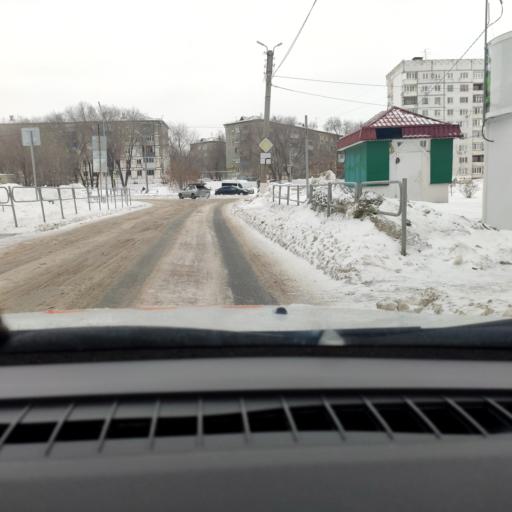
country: RU
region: Samara
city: Novokuybyshevsk
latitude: 53.0895
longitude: 49.9759
